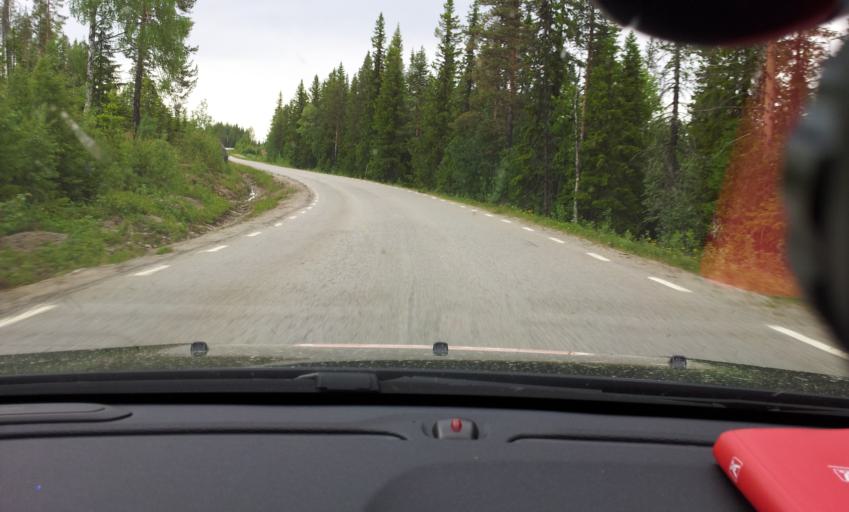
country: SE
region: Jaemtland
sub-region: Bergs Kommun
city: Hoverberg
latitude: 62.6918
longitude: 14.6313
